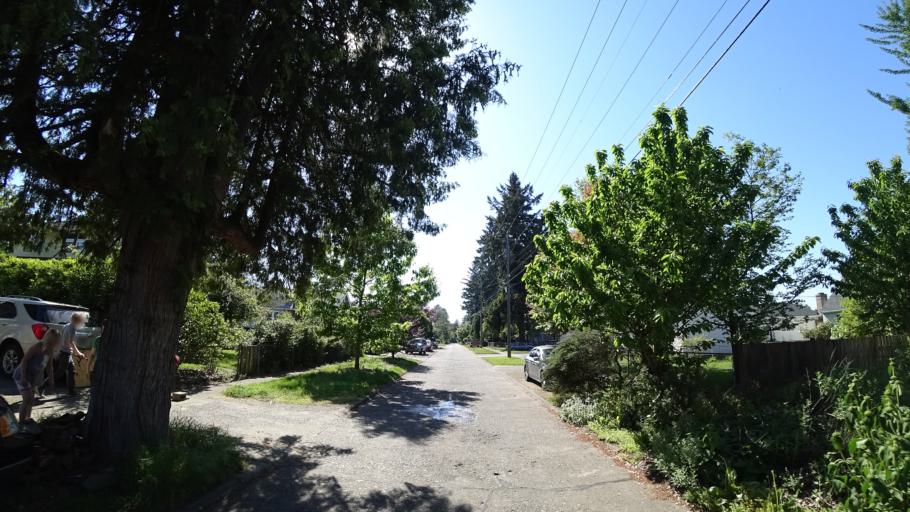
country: US
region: Oregon
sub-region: Multnomah County
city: Lents
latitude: 45.4879
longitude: -122.6050
